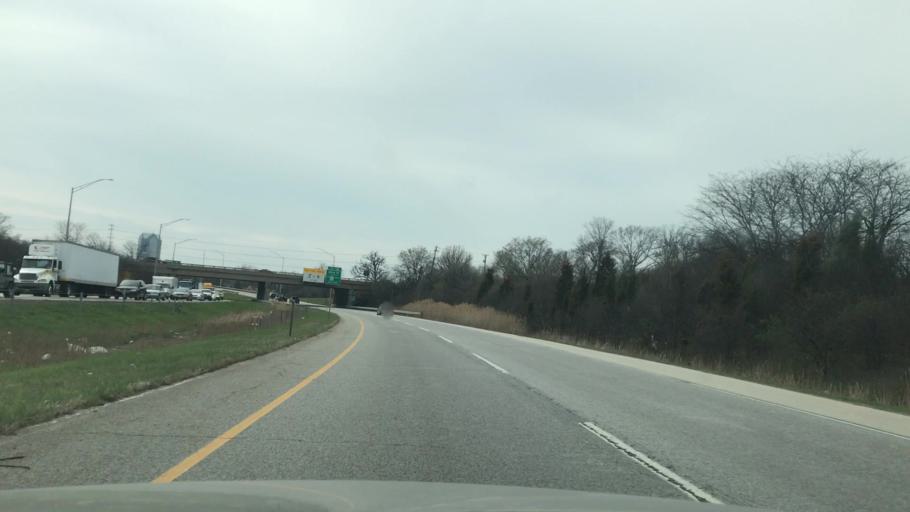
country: US
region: Illinois
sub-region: DuPage County
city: Oak Brook
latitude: 41.8526
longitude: -87.9275
